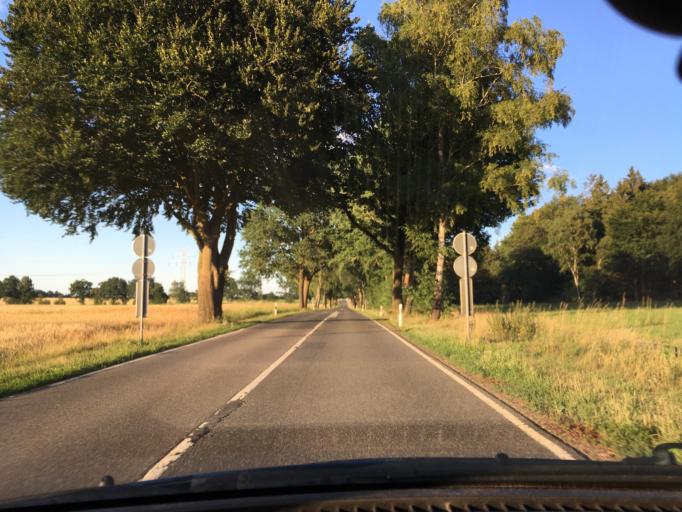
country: DE
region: Lower Saxony
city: Eyendorf
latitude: 53.1991
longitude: 10.1213
